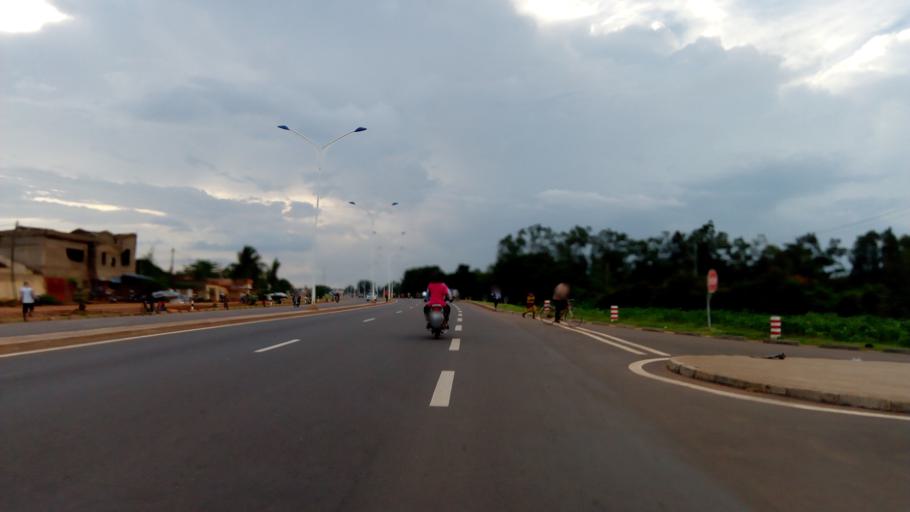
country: TG
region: Maritime
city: Lome
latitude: 6.2444
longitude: 1.1921
